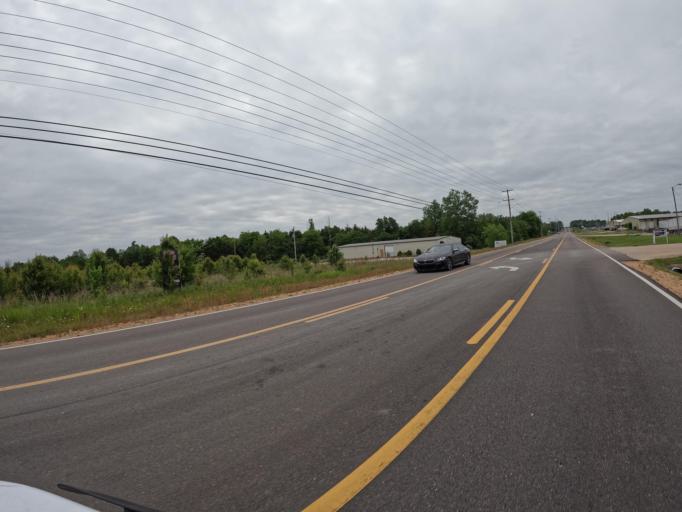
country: US
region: Mississippi
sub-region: Lee County
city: Tupelo
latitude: 34.2779
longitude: -88.7643
